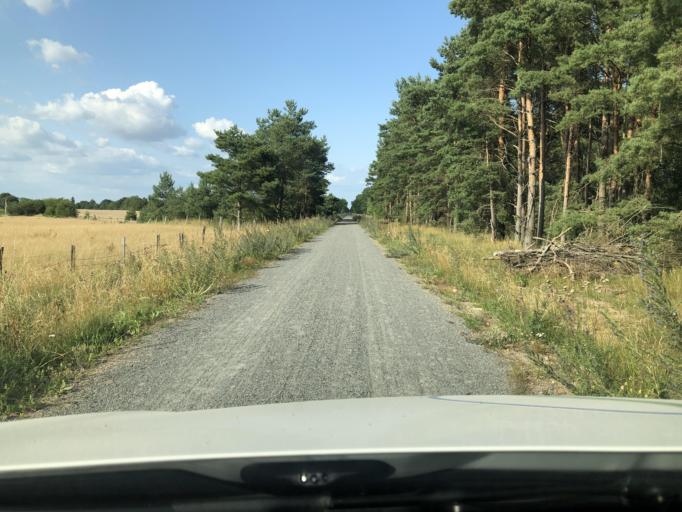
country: SE
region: Skane
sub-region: Kristianstads Kommun
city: Norra Asum
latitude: 55.9350
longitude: 14.1375
